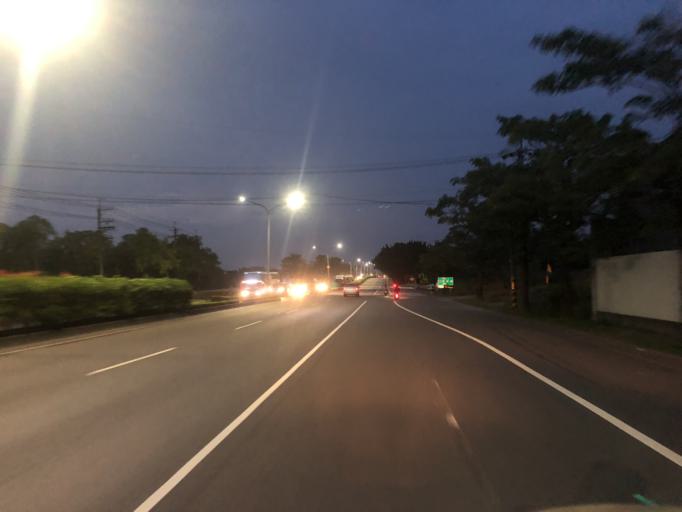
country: TW
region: Taiwan
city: Yujing
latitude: 23.1673
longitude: 120.3402
